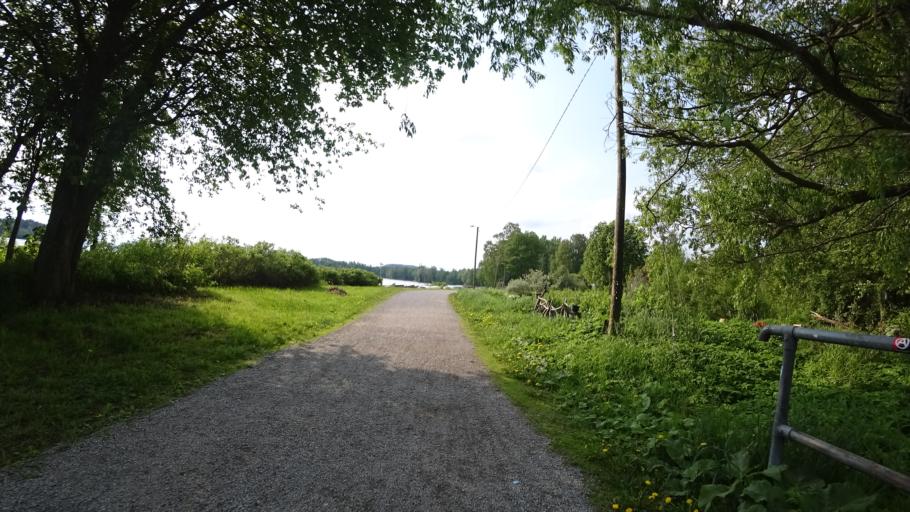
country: FI
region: Pirkanmaa
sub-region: Tampere
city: Tampere
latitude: 61.5006
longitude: 23.7083
